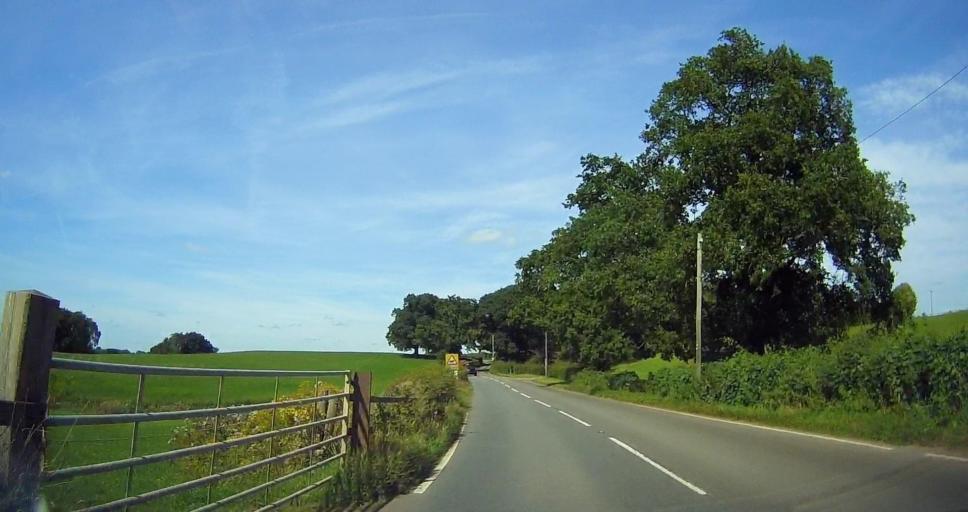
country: GB
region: England
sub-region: Shropshire
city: Market Drayton
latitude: 52.9632
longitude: -2.5157
